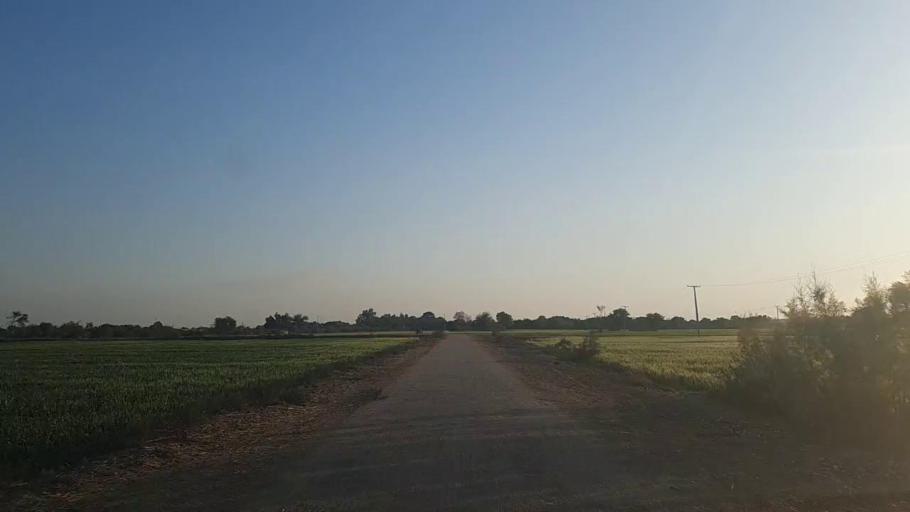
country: PK
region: Sindh
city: Jam Sahib
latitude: 26.3258
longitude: 68.6972
